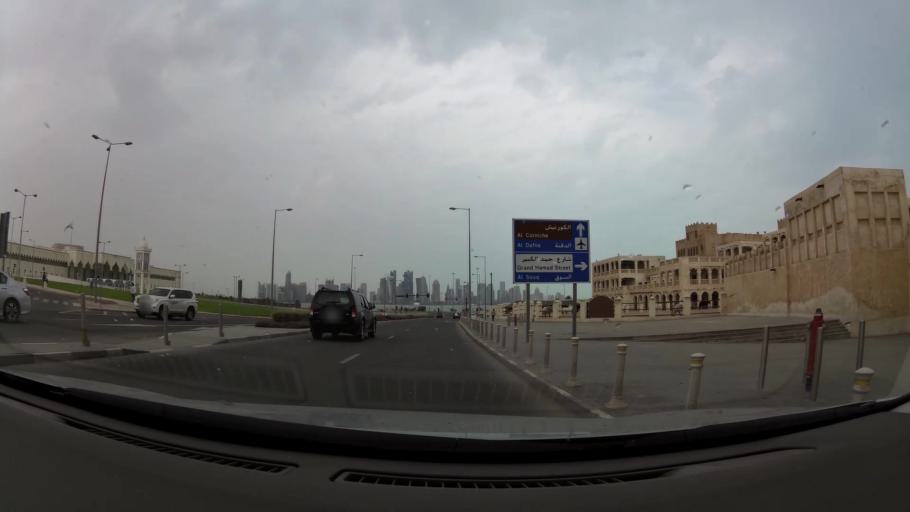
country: QA
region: Baladiyat ad Dawhah
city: Doha
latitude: 25.2892
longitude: 51.5300
